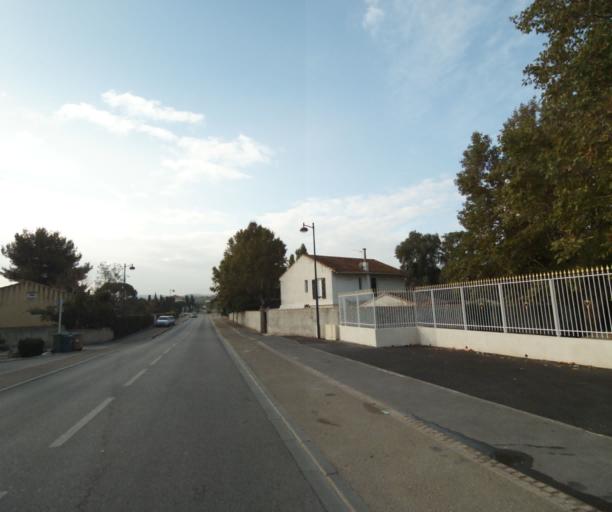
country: FR
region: Provence-Alpes-Cote d'Azur
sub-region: Departement des Bouches-du-Rhone
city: Saint-Victoret
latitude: 43.4206
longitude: 5.2446
